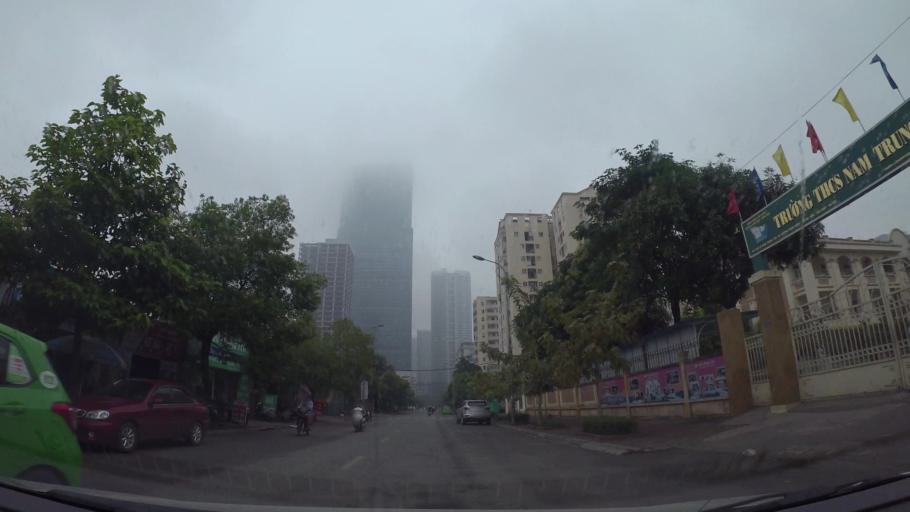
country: VN
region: Ha Noi
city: Thanh Xuan
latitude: 21.0135
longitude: 105.7878
